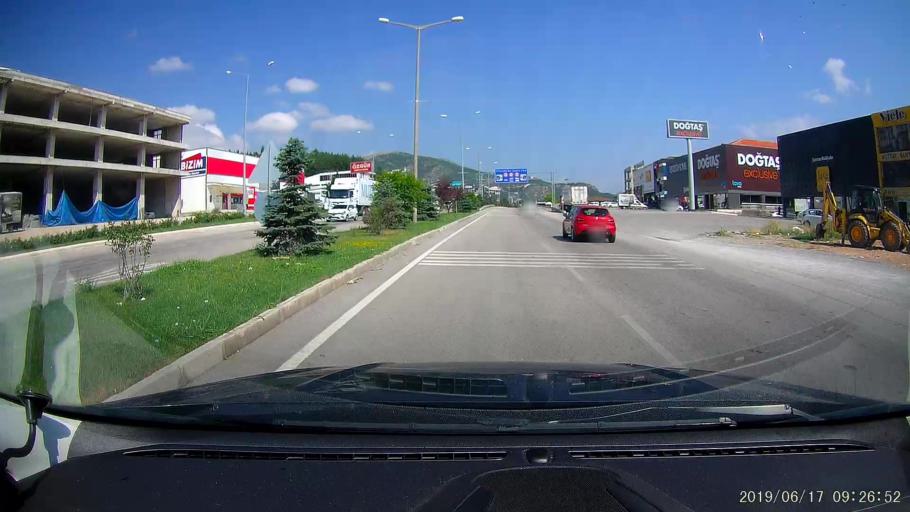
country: TR
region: Amasya
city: Amasya
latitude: 40.6718
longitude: 35.8311
